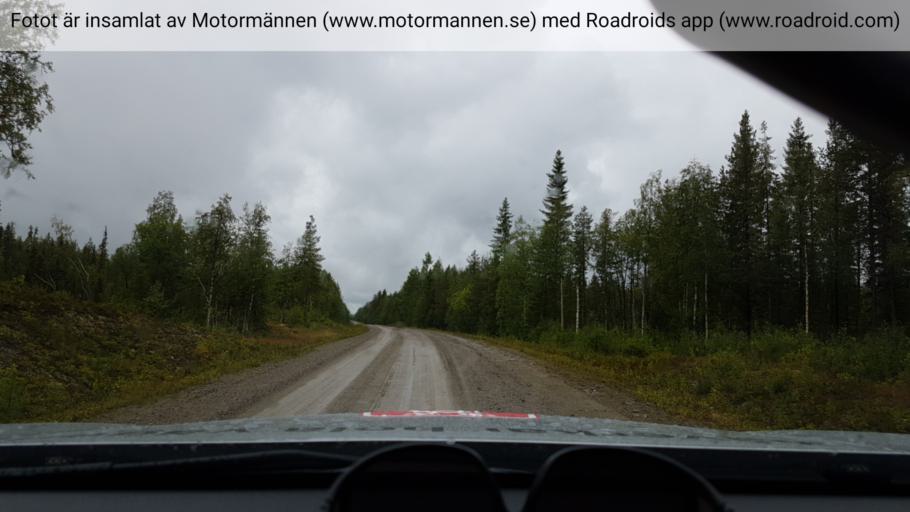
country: SE
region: Vaesterbotten
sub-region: Asele Kommun
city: Insjon
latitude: 64.7884
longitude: 17.6249
